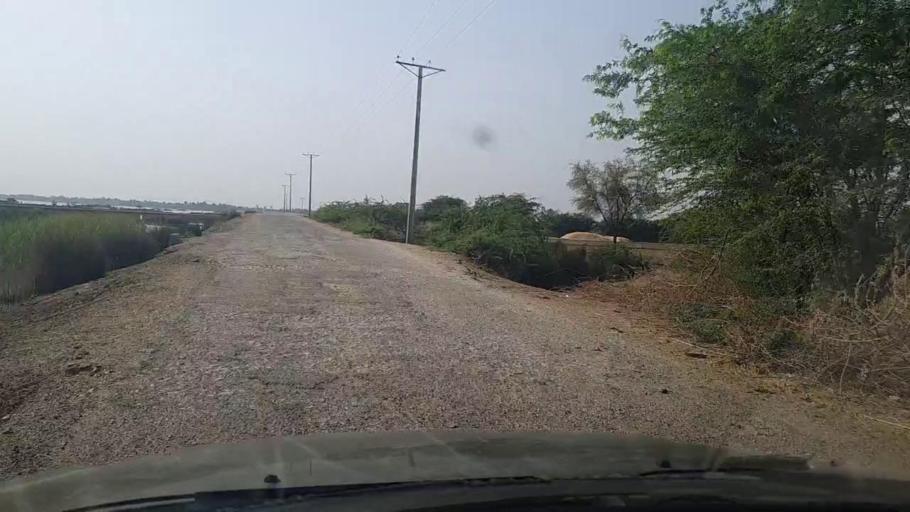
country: PK
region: Sindh
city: Kot Diji
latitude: 27.2915
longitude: 68.6453
